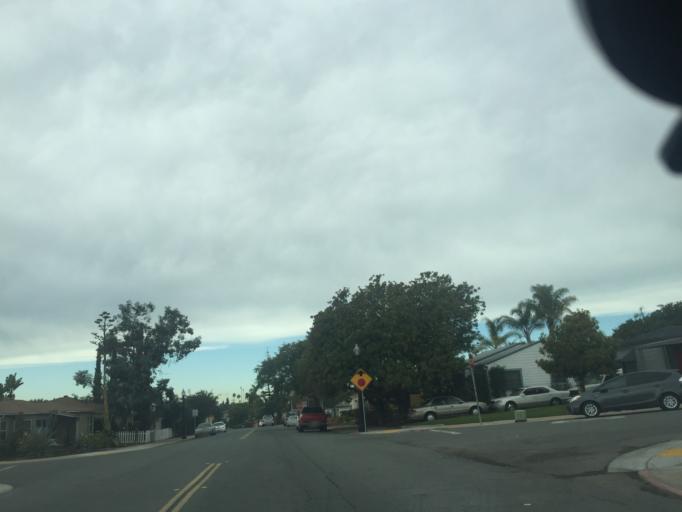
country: US
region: California
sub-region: San Diego County
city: Lemon Grove
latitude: 32.7593
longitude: -117.0907
